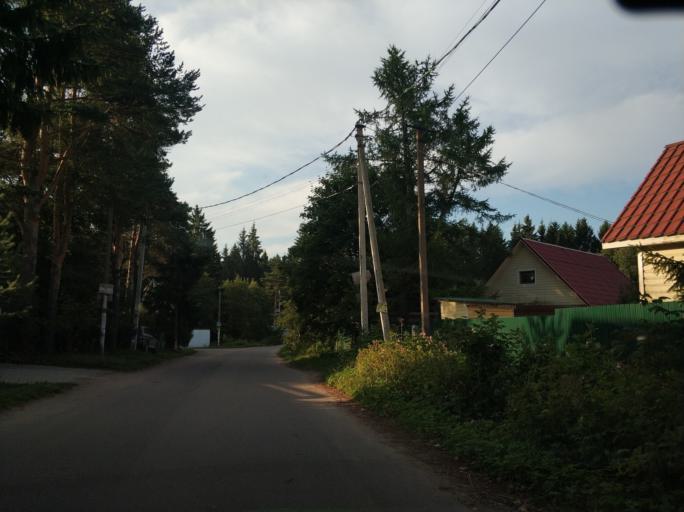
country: RU
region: Leningrad
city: Shcheglovo
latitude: 60.0525
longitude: 30.7450
